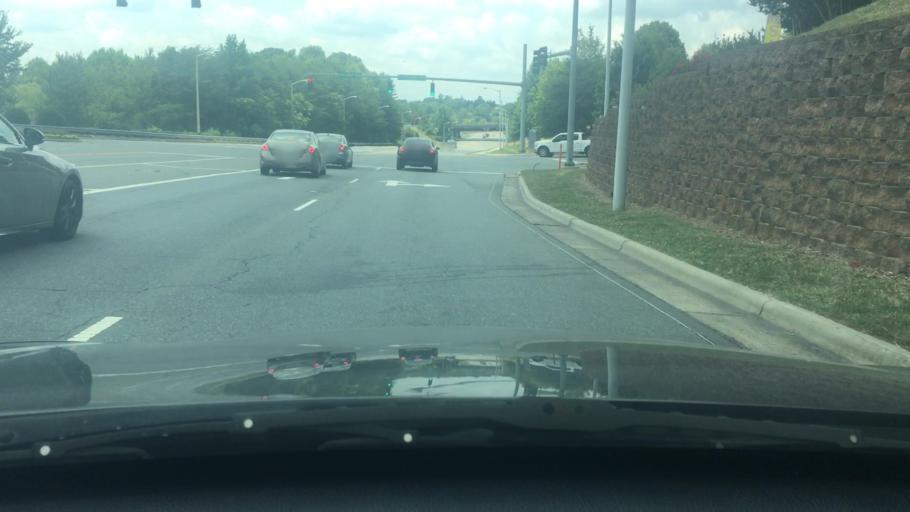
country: US
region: North Carolina
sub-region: Forsyth County
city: Winston-Salem
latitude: 36.0681
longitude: -80.2979
